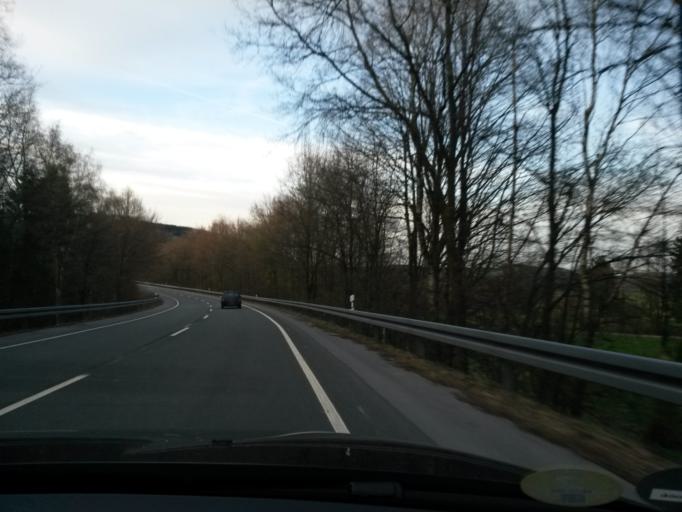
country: DE
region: North Rhine-Westphalia
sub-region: Regierungsbezirk Arnsberg
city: Herscheid
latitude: 51.1542
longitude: 7.7432
